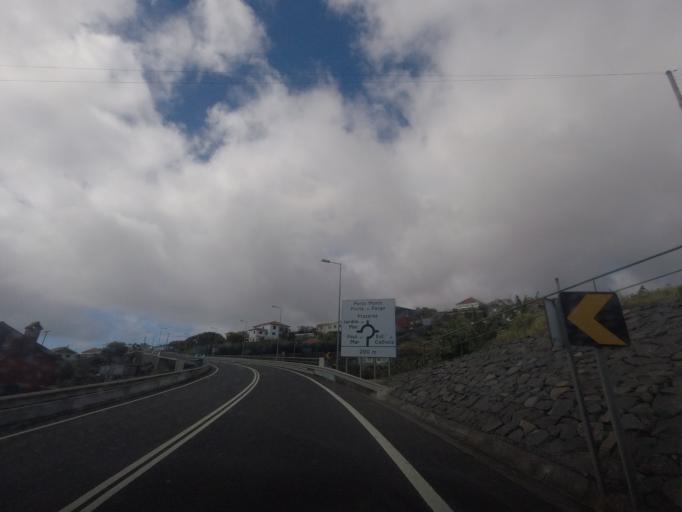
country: PT
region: Madeira
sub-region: Calheta
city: Estreito da Calheta
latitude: 32.7321
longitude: -17.1905
